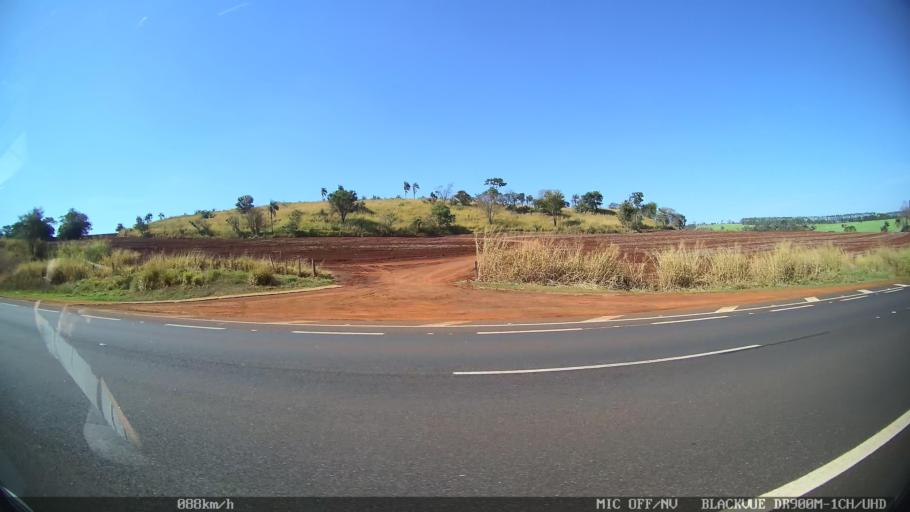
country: BR
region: Sao Paulo
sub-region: Franca
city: Franca
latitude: -20.6128
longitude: -47.4556
